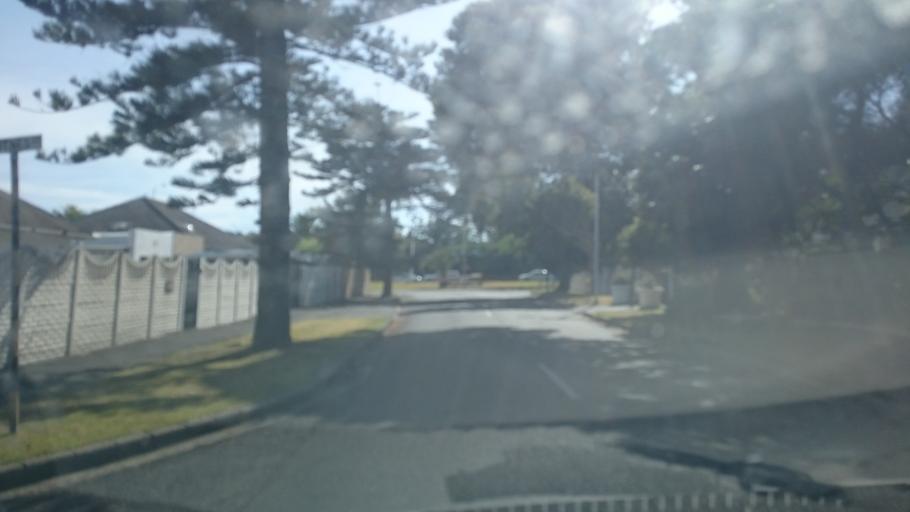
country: ZA
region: Western Cape
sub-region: City of Cape Town
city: Lansdowne
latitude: -34.0172
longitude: 18.4839
